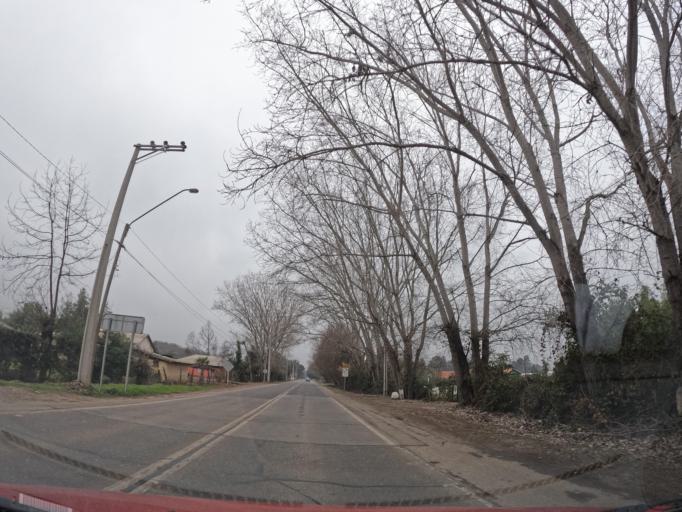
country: CL
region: Maule
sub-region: Provincia de Talca
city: San Clemente
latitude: -35.5598
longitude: -71.4623
